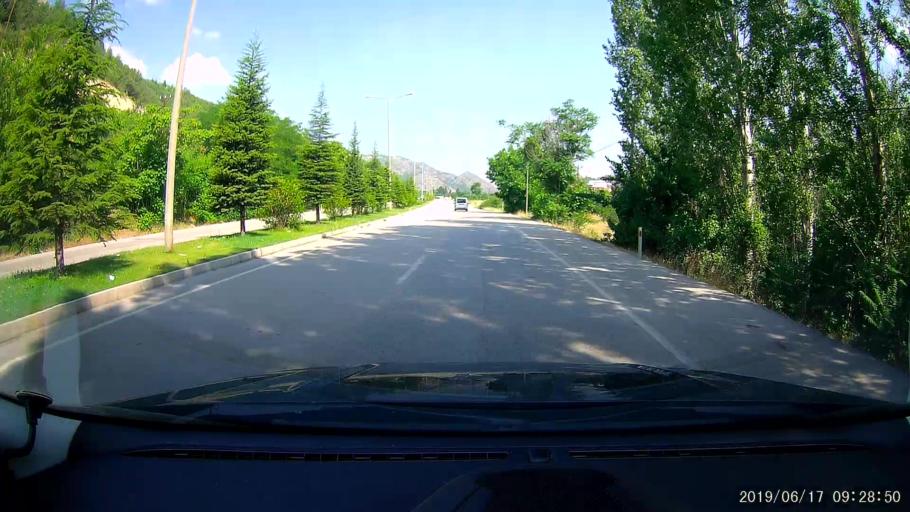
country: TR
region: Amasya
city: Amasya
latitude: 40.6926
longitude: 35.8197
